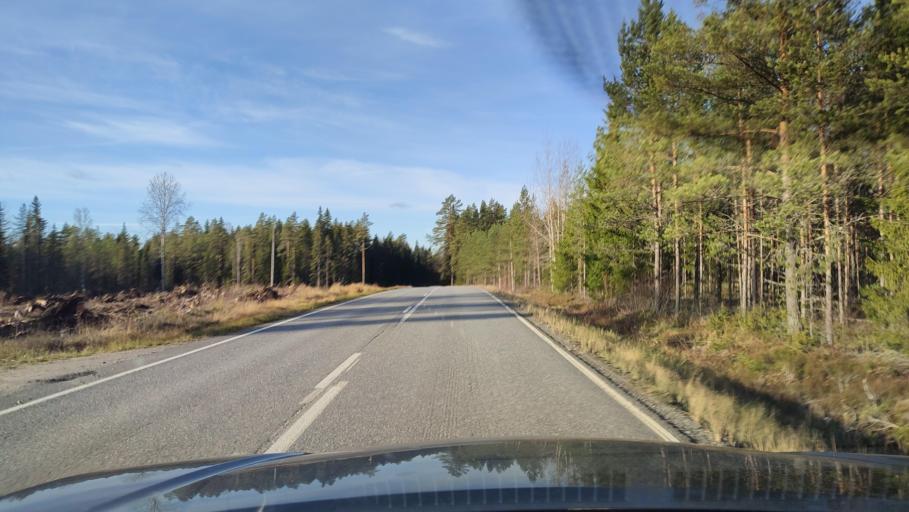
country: FI
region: Ostrobothnia
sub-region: Sydosterbotten
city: Naerpes
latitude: 62.4633
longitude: 21.5187
